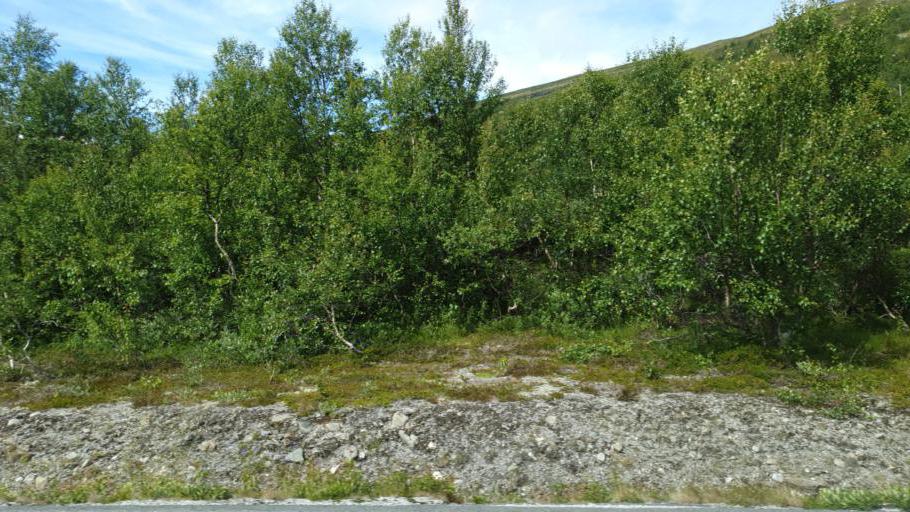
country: NO
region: Oppland
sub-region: Vaga
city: Vagamo
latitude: 61.5188
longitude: 8.8638
